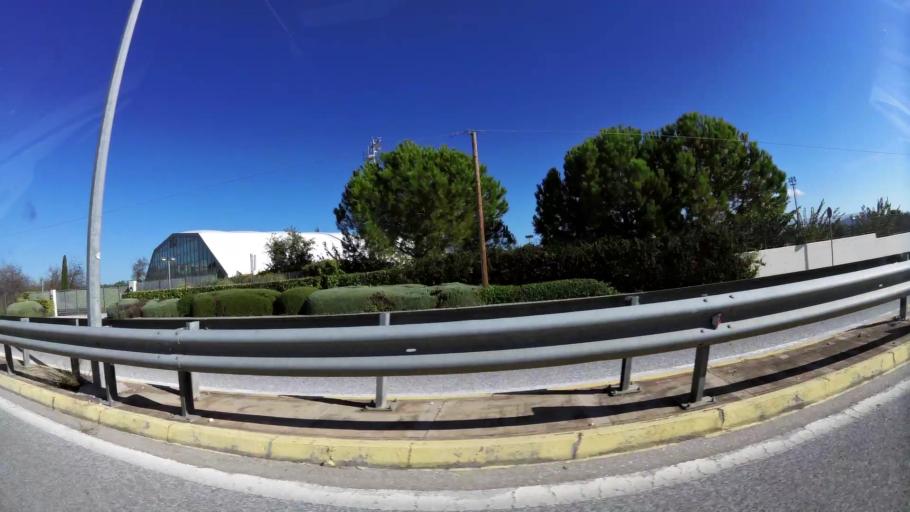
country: GR
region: Attica
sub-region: Nomarchia Anatolikis Attikis
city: Pallini
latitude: 37.9971
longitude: 23.8910
